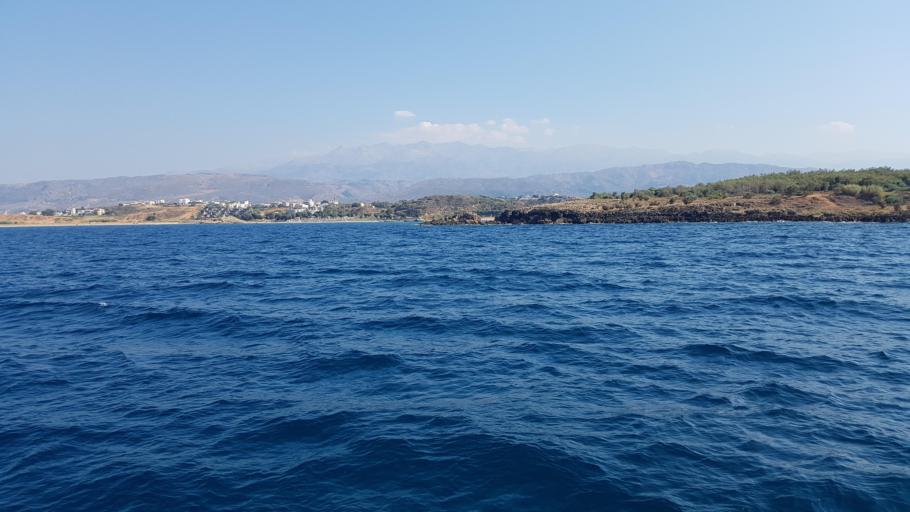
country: GR
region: Crete
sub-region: Nomos Chanias
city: Daratsos
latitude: 35.5198
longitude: 23.9901
